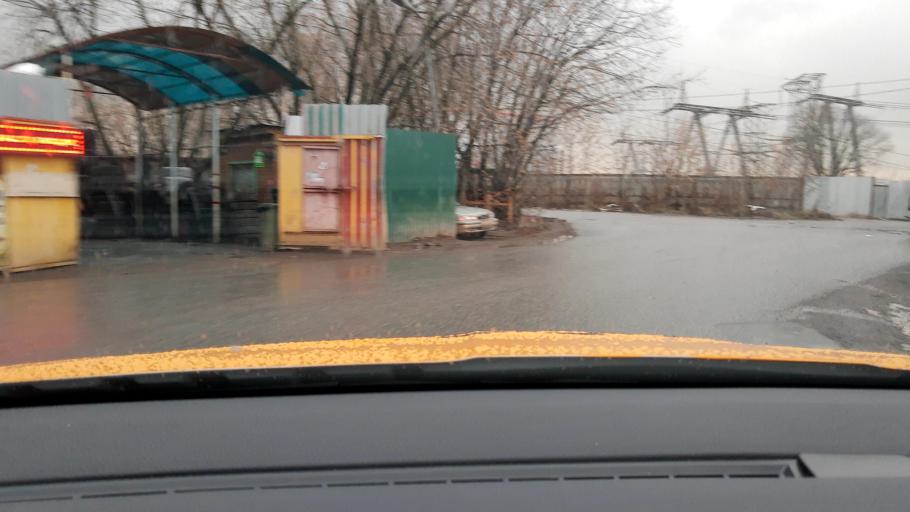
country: RU
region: Moscow
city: Kapotnya
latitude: 55.6596
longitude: 37.8007
